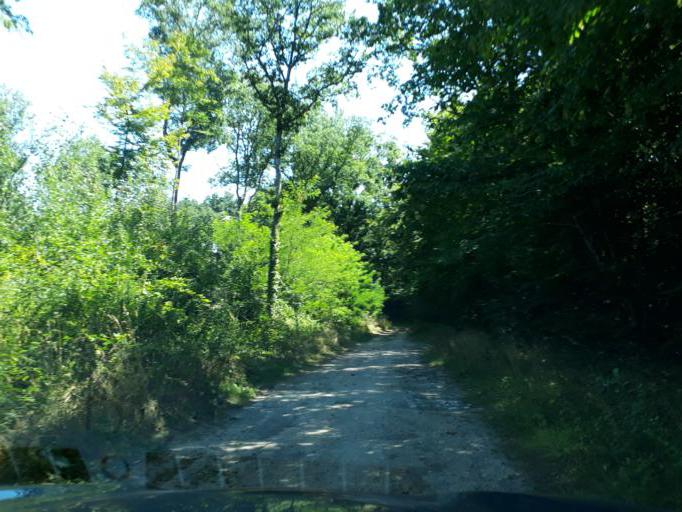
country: FR
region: Centre
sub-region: Departement du Loiret
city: Chevilly
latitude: 47.9906
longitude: 1.8909
